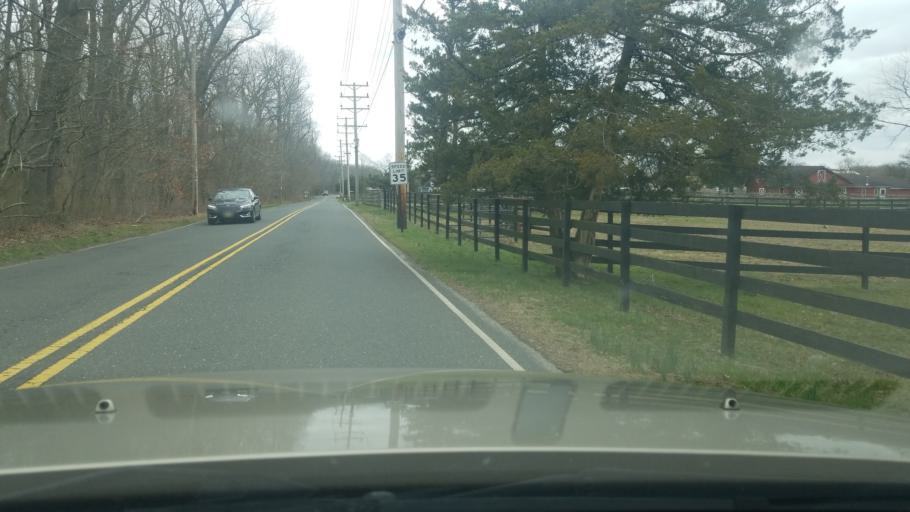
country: US
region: New Jersey
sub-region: Monmouth County
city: Ramtown
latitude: 40.1403
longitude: -74.1542
